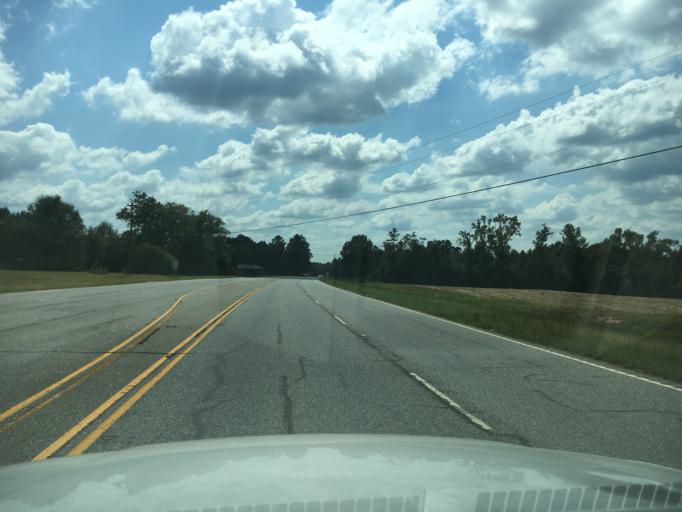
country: US
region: South Carolina
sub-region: Greenwood County
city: Ware Shoals
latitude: 34.4493
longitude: -82.2510
